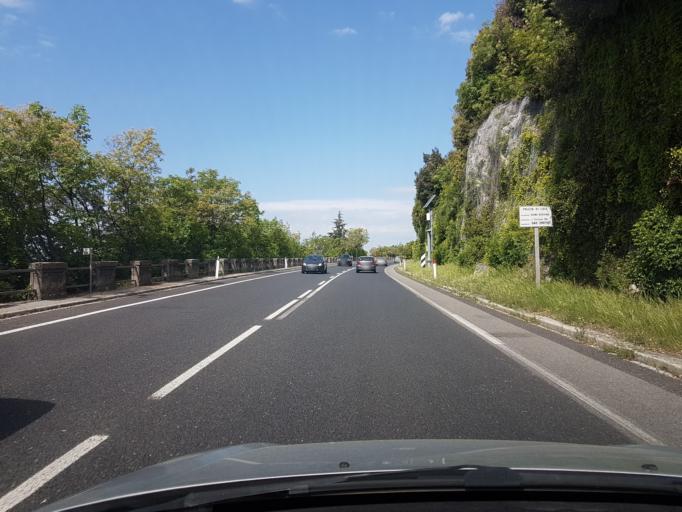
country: IT
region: Friuli Venezia Giulia
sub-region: Provincia di Trieste
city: Aurisina Cave
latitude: 45.7565
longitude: 13.6463
